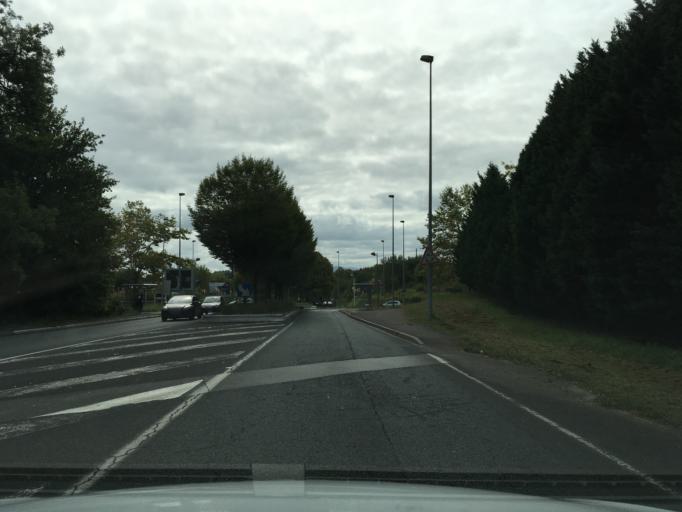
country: FR
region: Aquitaine
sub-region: Departement des Pyrenees-Atlantiques
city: Bayonne
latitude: 43.4796
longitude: -1.4563
